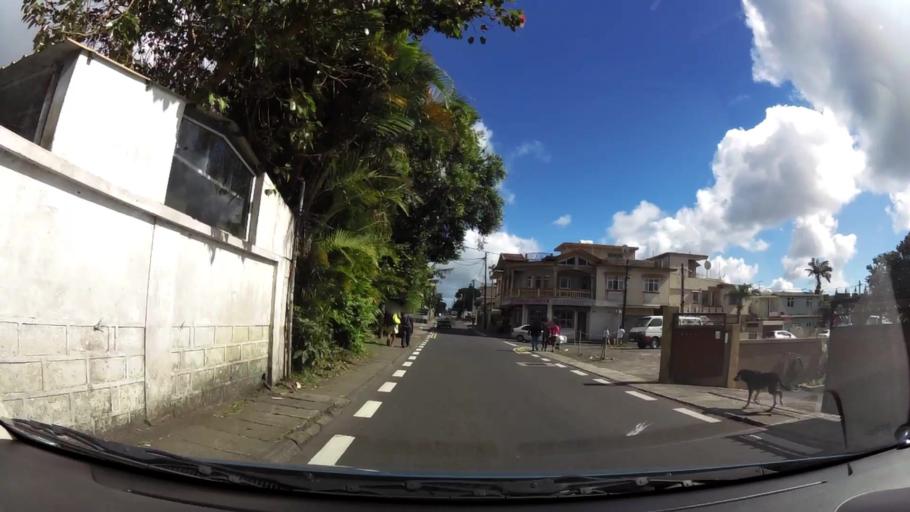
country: MU
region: Plaines Wilhems
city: Curepipe
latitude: -20.3299
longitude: 57.5258
